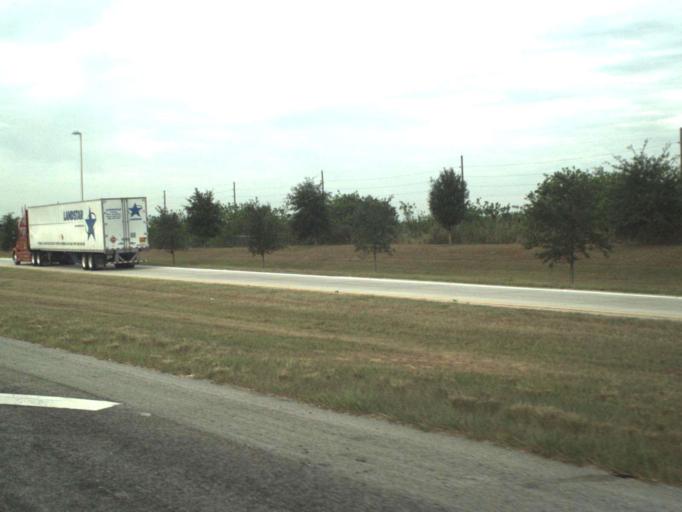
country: US
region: Florida
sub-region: Saint Lucie County
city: Port Saint Lucie
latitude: 27.1948
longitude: -80.4005
